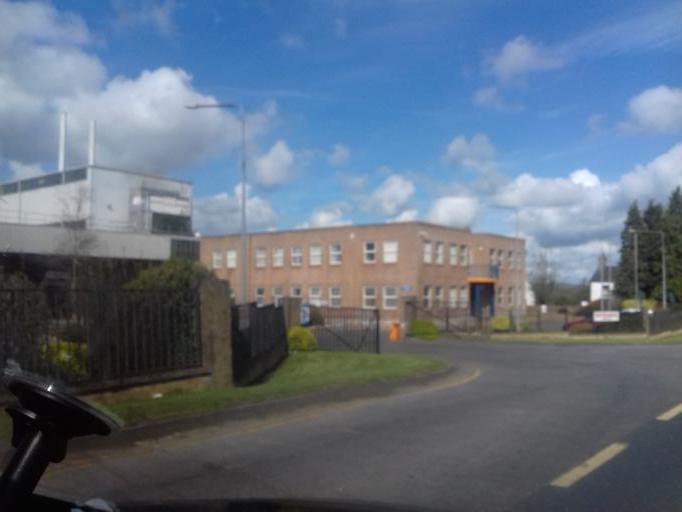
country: IE
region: Ulster
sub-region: An Cabhan
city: Virginia
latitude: 53.8154
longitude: -7.0500
